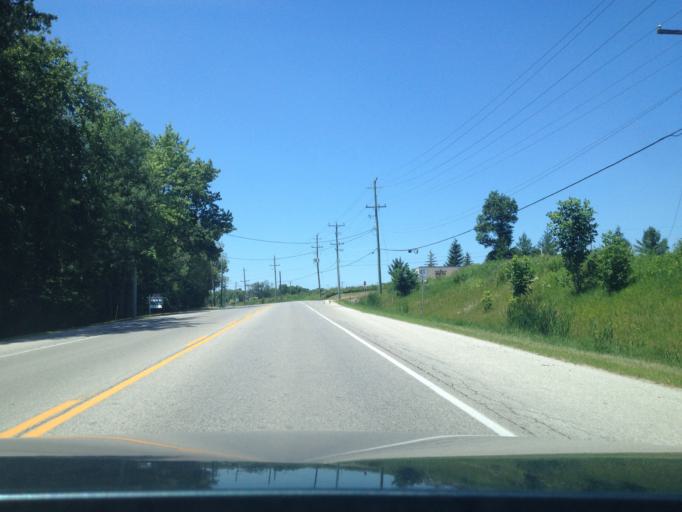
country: CA
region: Ontario
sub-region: Wellington County
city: Guelph
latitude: 43.6922
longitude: -80.4019
